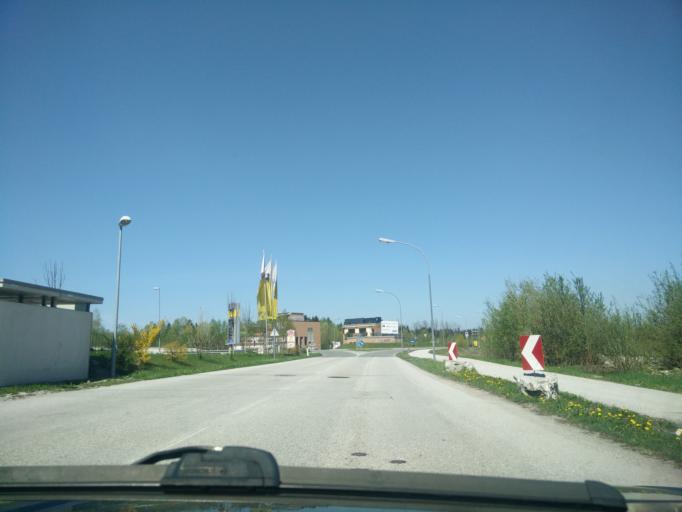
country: AT
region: Salzburg
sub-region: Politischer Bezirk Hallein
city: Puch bei Hallein
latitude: 47.7323
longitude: 13.0870
